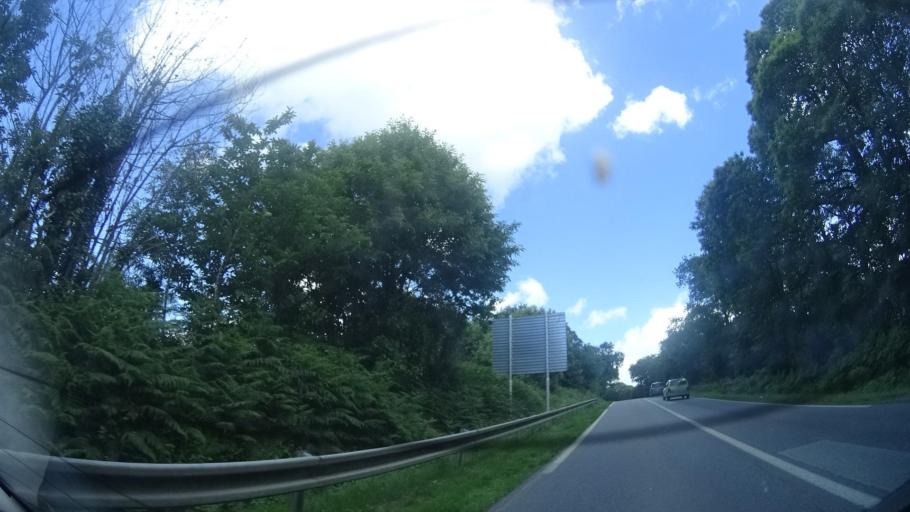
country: FR
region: Brittany
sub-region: Departement du Morbihan
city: Questembert
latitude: 47.6796
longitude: -2.4199
